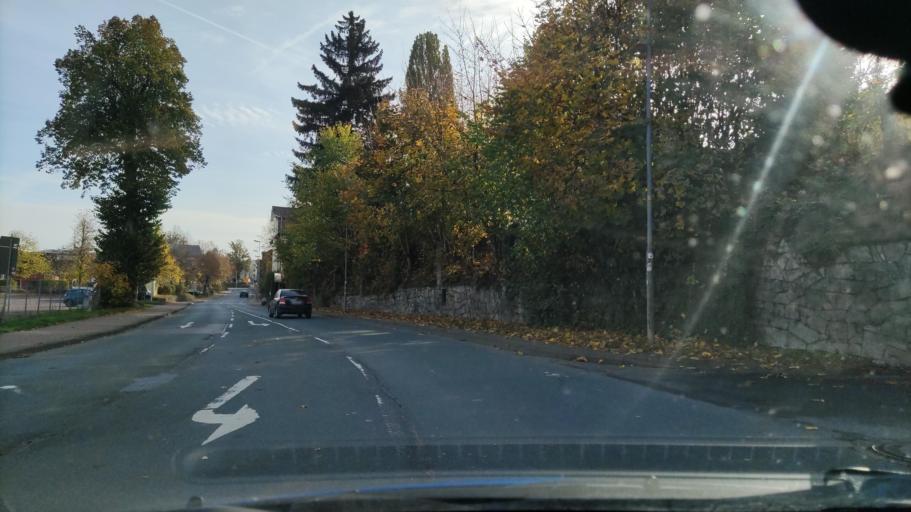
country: DE
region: Lower Saxony
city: Stadtoldendorf
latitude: 51.8841
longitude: 9.6196
